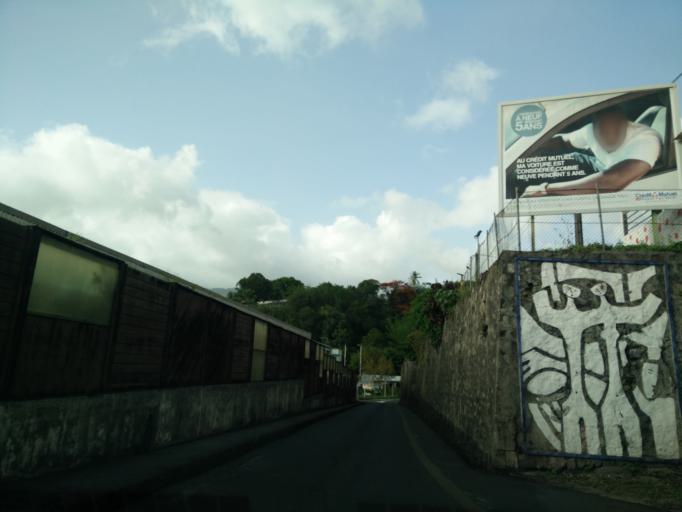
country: MQ
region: Martinique
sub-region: Martinique
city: Saint-Pierre
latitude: 14.7482
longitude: -61.1766
